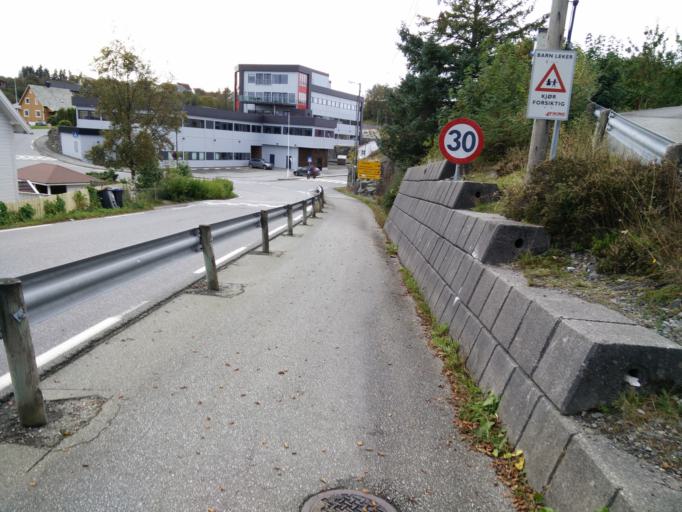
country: NO
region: Hordaland
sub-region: Sveio
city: Sveio
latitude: 59.6026
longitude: 5.2087
